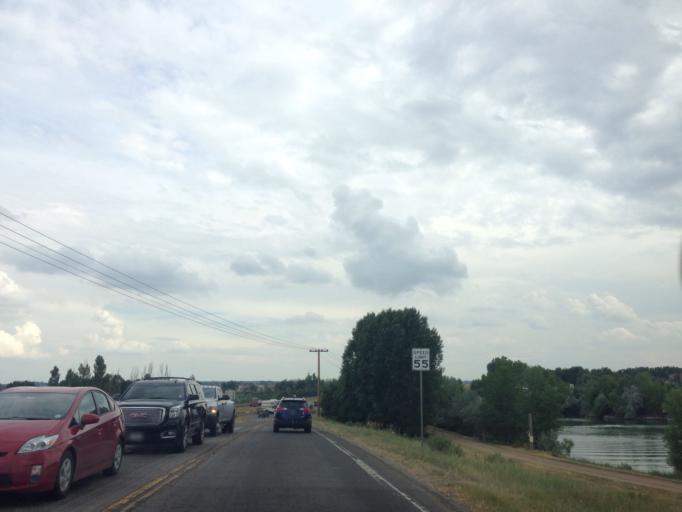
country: US
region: Colorado
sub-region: Weld County
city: Windsor
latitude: 40.5085
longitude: -104.9924
